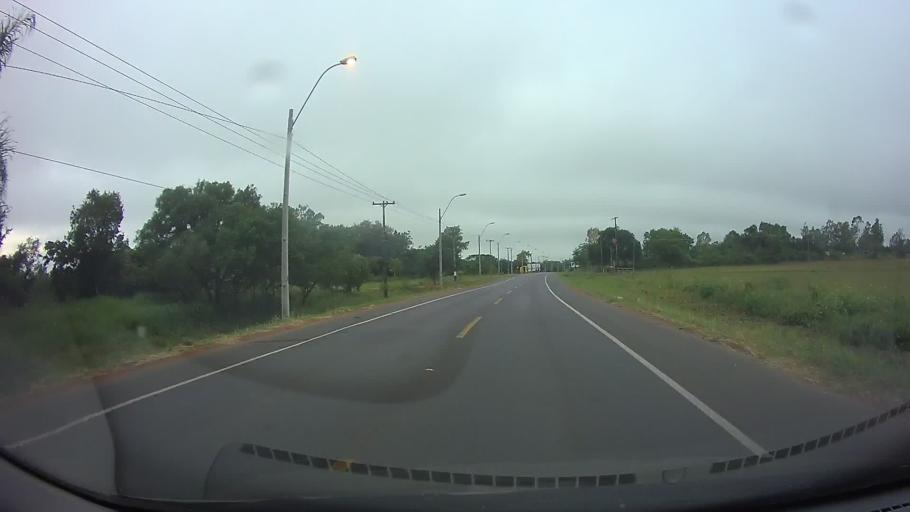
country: PY
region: Central
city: Itaugua
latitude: -25.3454
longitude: -57.3407
